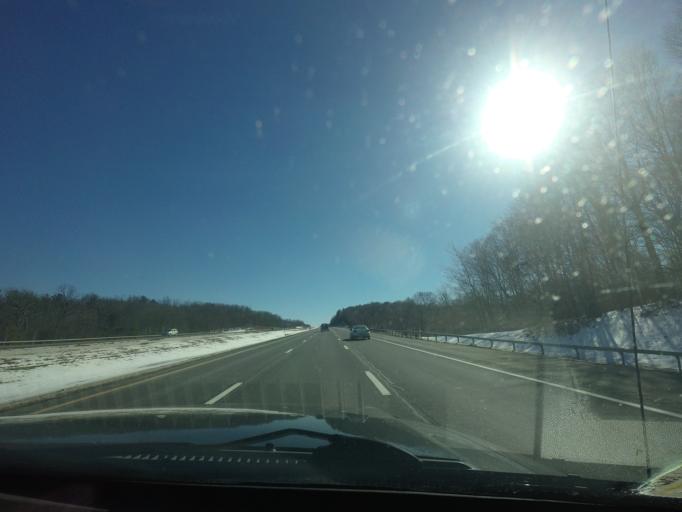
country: US
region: New York
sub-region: Rensselaer County
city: East Greenbush
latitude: 42.6158
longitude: -73.6895
